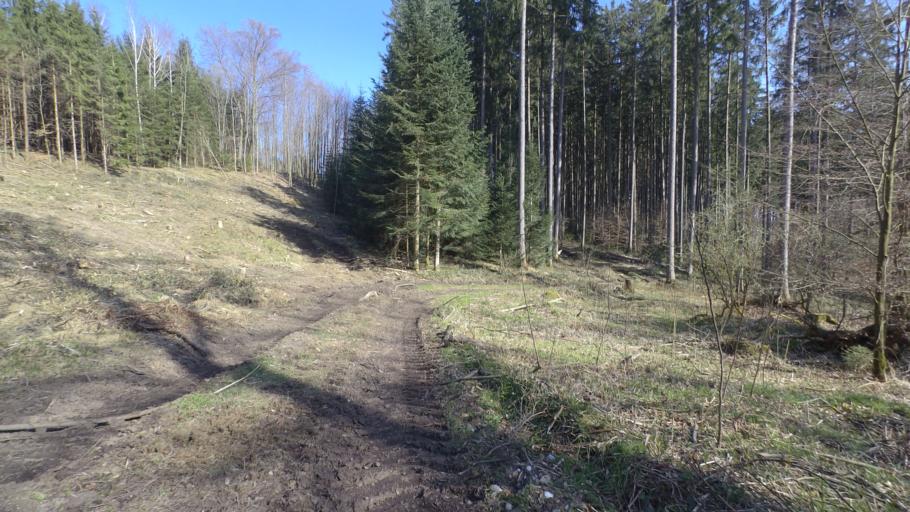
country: DE
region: Bavaria
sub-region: Upper Bavaria
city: Nussdorf
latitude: 47.9090
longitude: 12.5721
